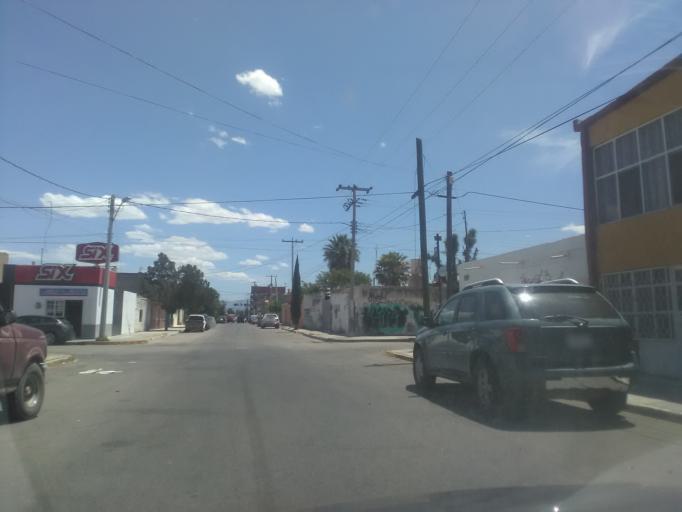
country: MX
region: Durango
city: Victoria de Durango
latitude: 24.0344
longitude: -104.6351
